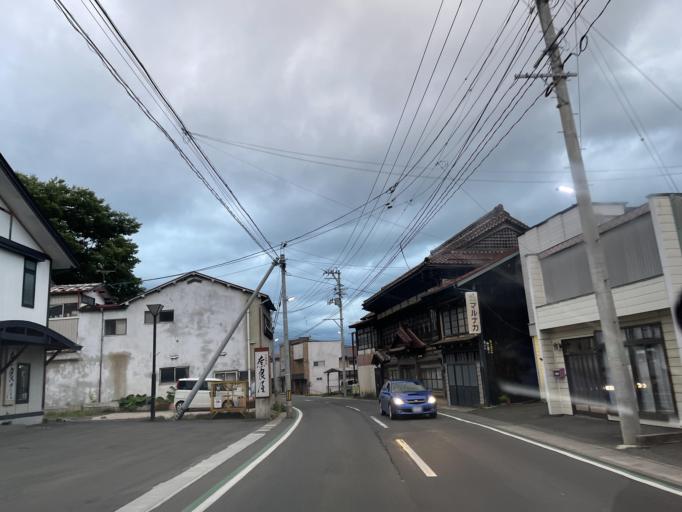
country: JP
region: Iwate
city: Ichinohe
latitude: 39.9701
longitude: 141.2224
